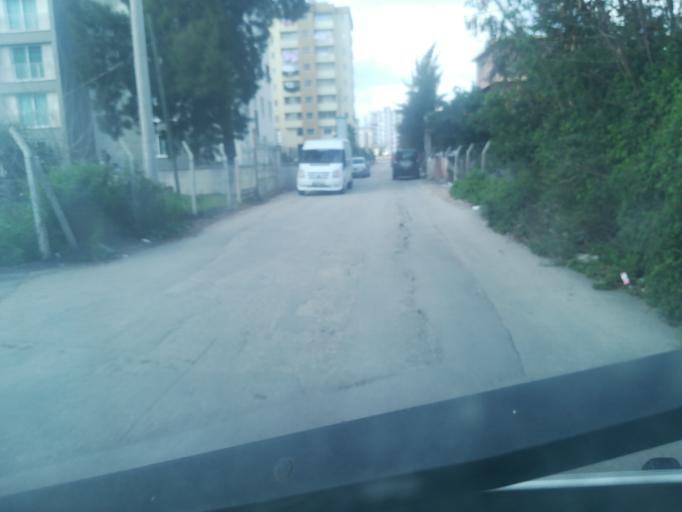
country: TR
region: Adana
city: Seyhan
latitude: 37.0074
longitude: 35.2701
